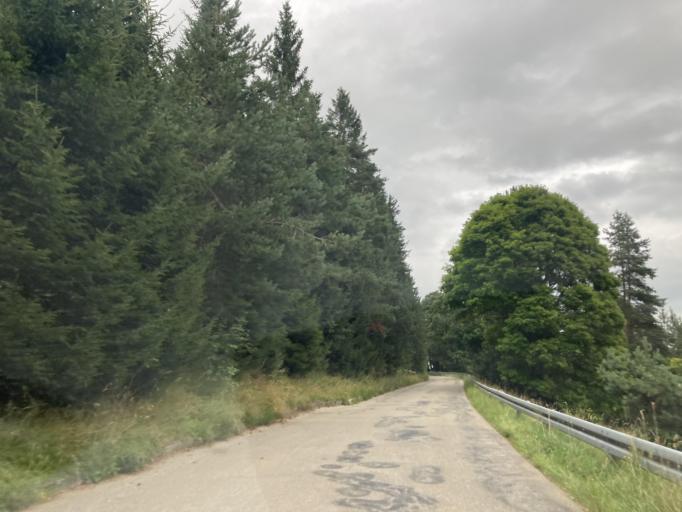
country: DE
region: Baden-Wuerttemberg
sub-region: Freiburg Region
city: Schonwald im Schwarzwald
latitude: 48.1149
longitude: 8.1972
